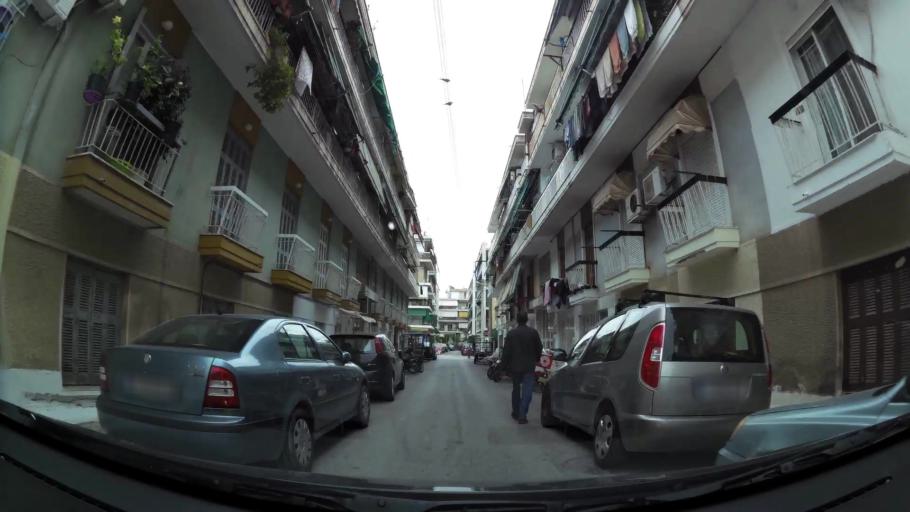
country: GR
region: Attica
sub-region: Nomos Piraios
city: Agios Ioannis Rentis
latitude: 37.9590
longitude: 23.6600
